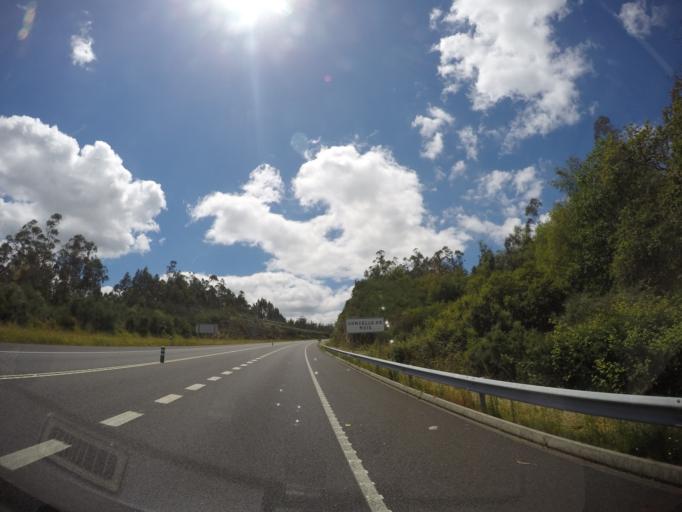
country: ES
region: Galicia
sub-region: Provincia da Coruna
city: Noia
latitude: 42.7651
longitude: -8.9407
